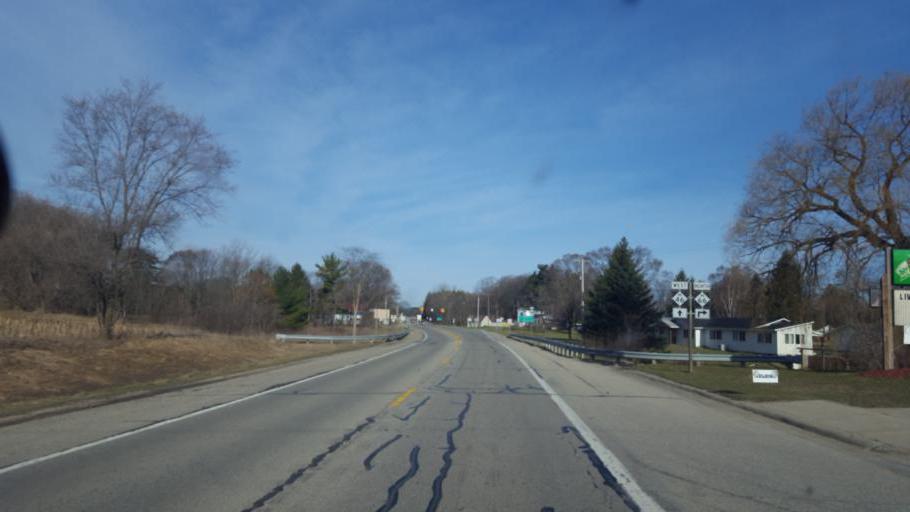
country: US
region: Michigan
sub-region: Montcalm County
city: Edmore
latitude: 43.4257
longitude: -85.1464
